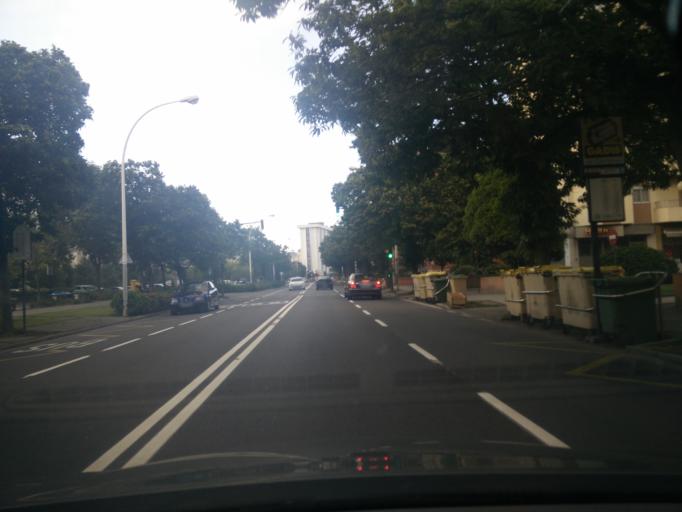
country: ES
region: Galicia
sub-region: Provincia da Coruna
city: A Coruna
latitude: 43.3461
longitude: -8.4065
